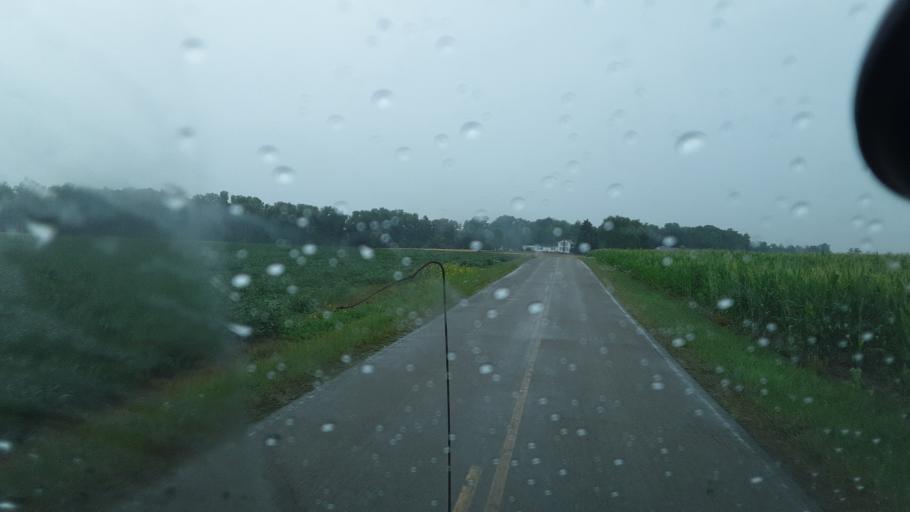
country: US
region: Ohio
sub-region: Williams County
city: Edgerton
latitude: 41.4260
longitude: -84.8015
